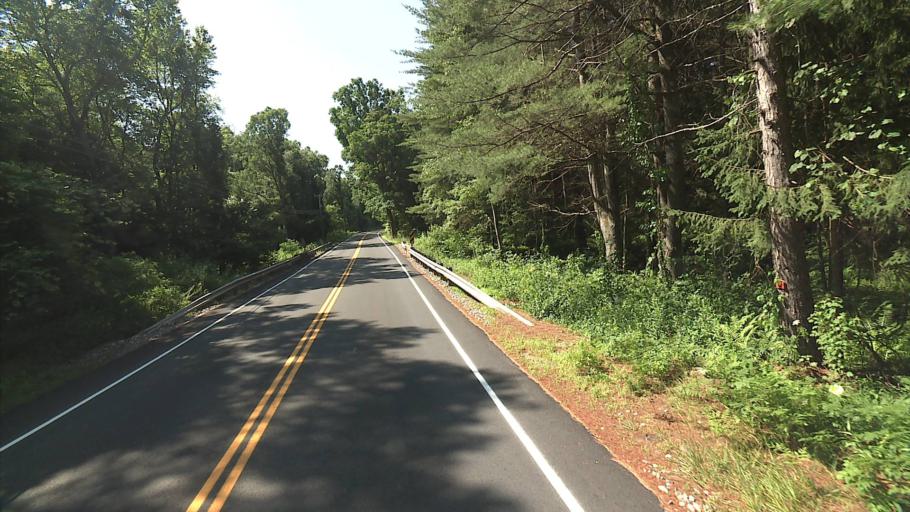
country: US
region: Connecticut
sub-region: Litchfield County
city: Terryville
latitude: 41.7304
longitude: -73.0143
